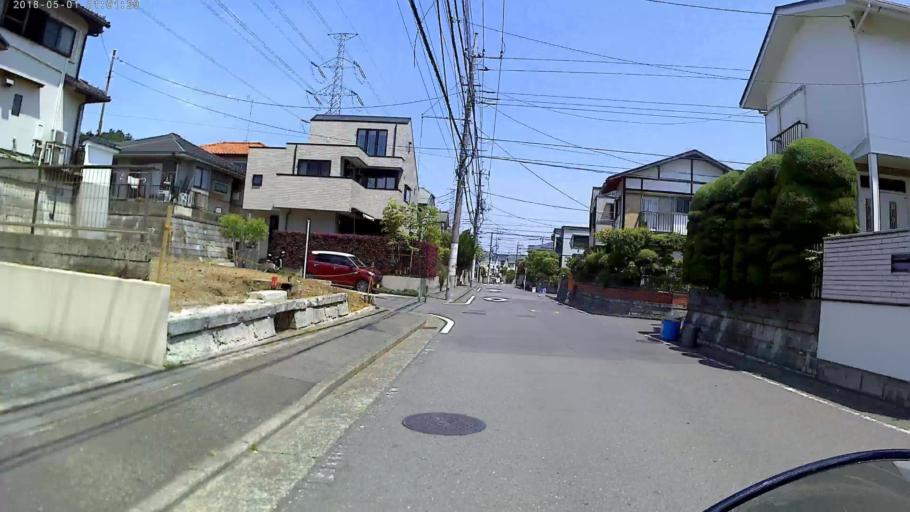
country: JP
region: Kanagawa
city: Minami-rinkan
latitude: 35.4778
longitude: 139.5174
